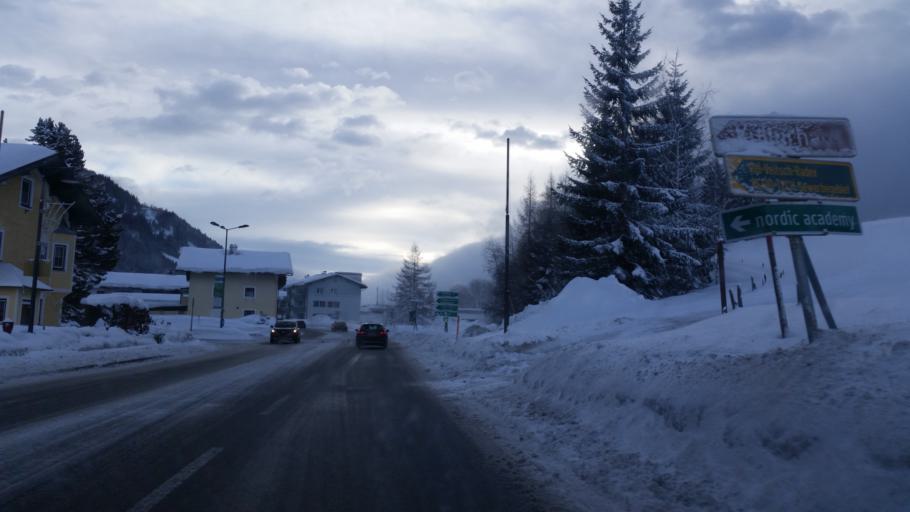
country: AT
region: Tyrol
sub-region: Politischer Bezirk Kitzbuhel
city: Hochfilzen
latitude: 47.4693
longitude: 12.6211
